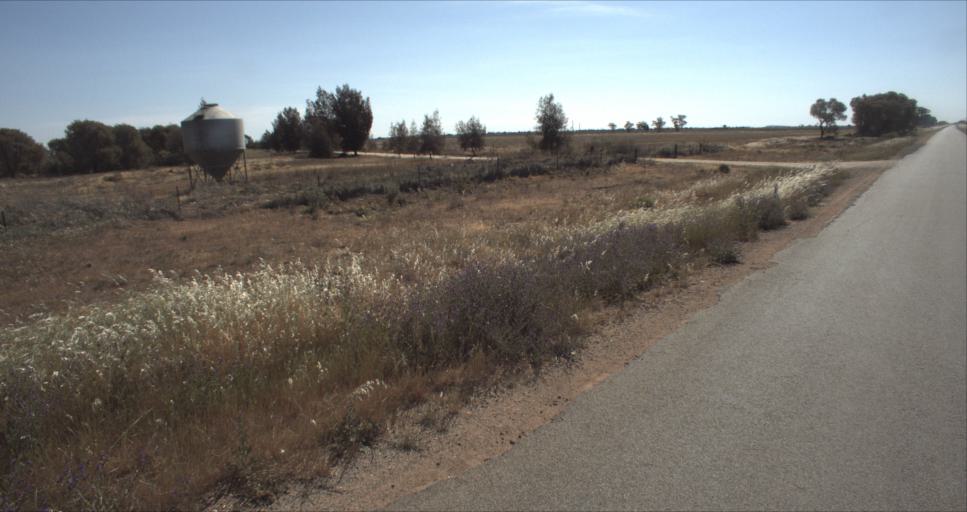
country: AU
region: New South Wales
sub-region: Leeton
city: Leeton
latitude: -34.4870
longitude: 146.3785
